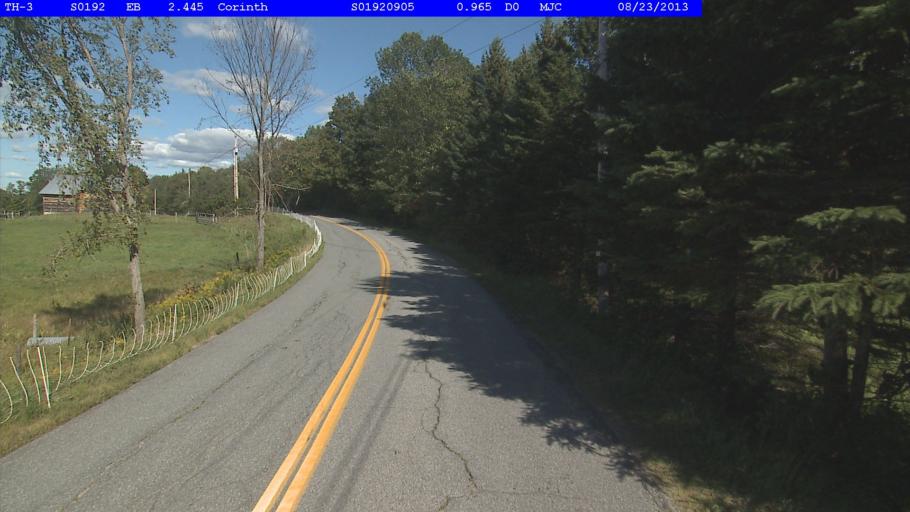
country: US
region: Vermont
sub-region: Orange County
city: Chelsea
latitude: 44.0041
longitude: -72.3379
